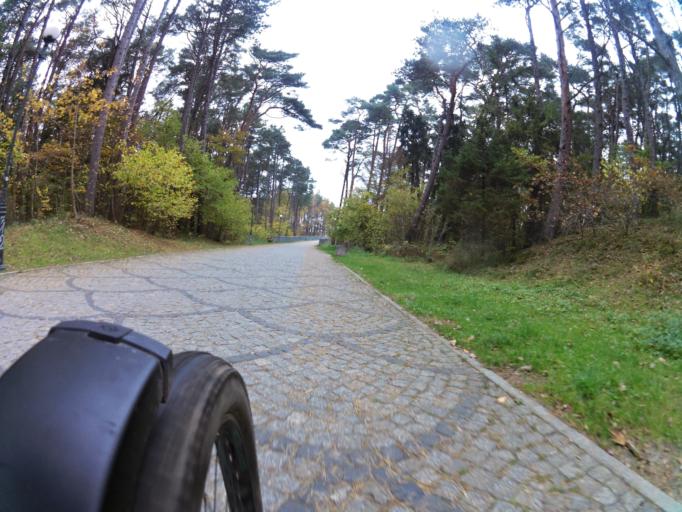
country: PL
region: Pomeranian Voivodeship
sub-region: Powiat pucki
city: Krokowa
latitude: 54.8310
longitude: 18.0883
